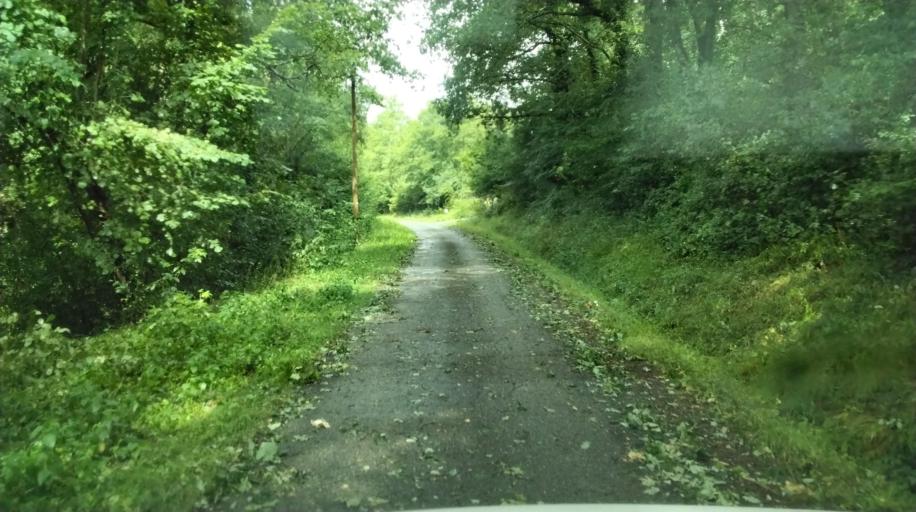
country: FR
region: Midi-Pyrenees
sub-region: Departement de la Haute-Garonne
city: Berat
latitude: 43.4211
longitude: 1.1677
